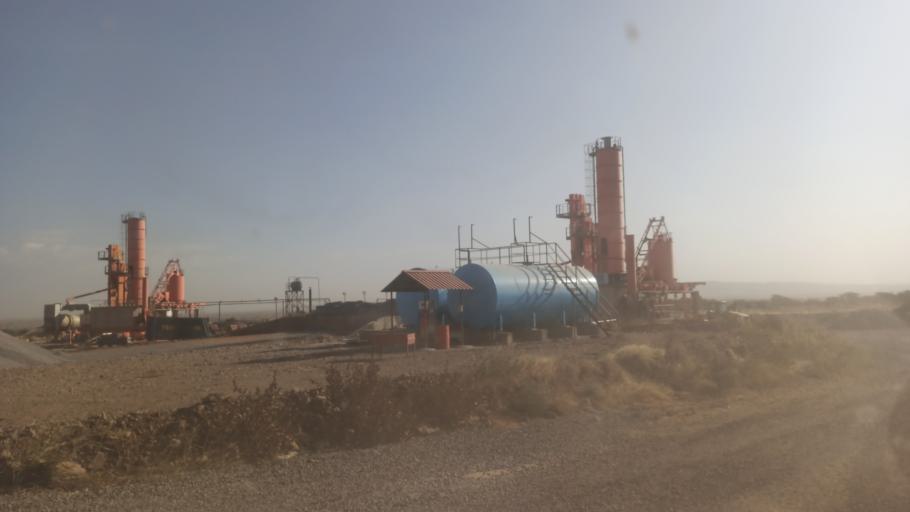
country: ET
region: Oromiya
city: Ziway
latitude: 7.9321
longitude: 38.6166
